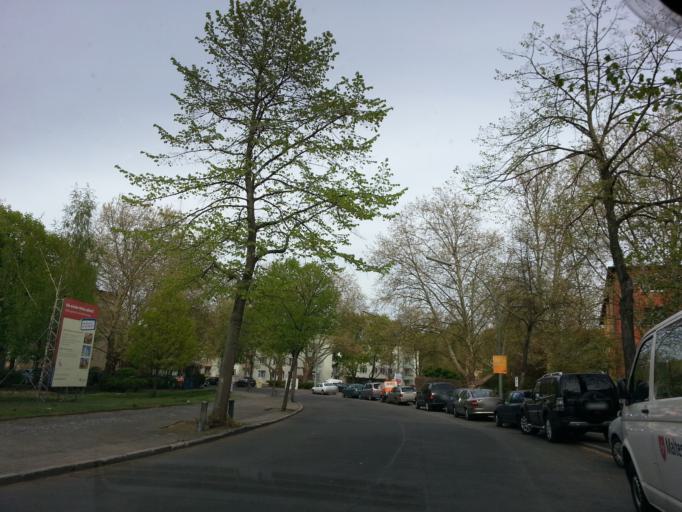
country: DE
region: Berlin
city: Charlottenburg-Nord
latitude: 52.5352
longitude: 13.2889
